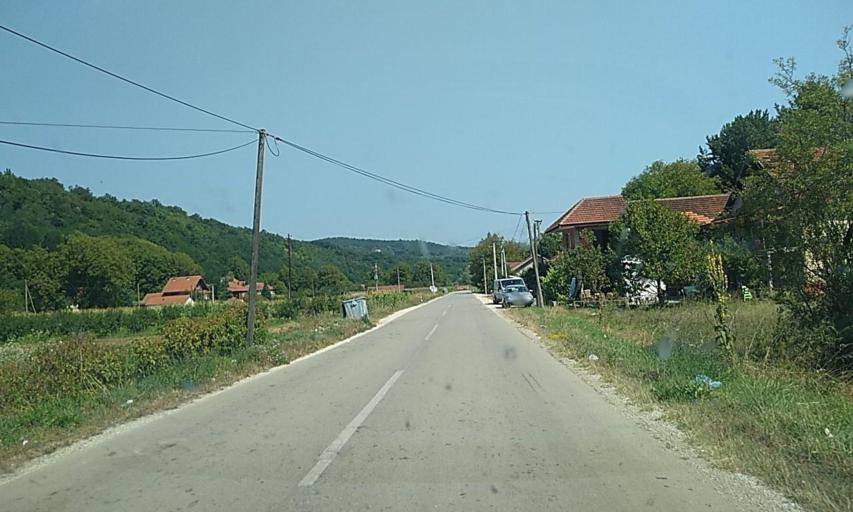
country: RS
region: Central Serbia
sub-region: Pcinjski Okrug
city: Vladicin Han
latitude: 42.6657
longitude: 22.0461
